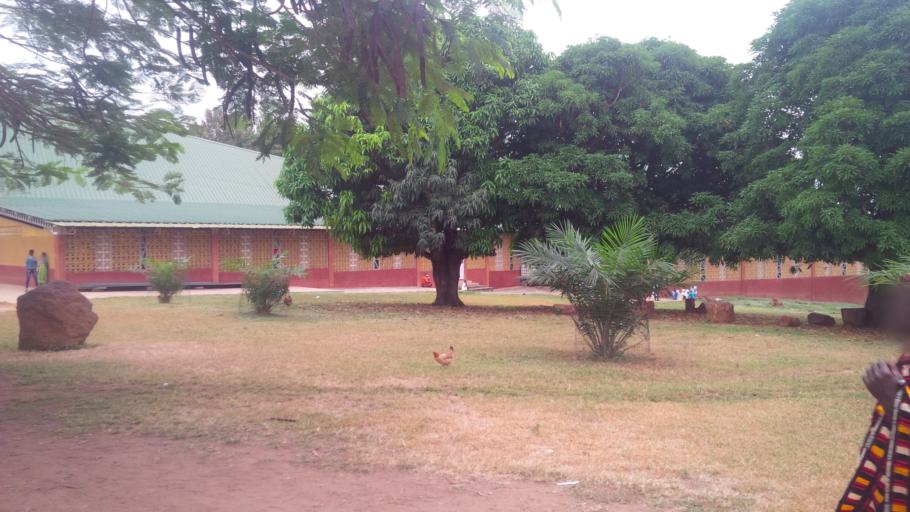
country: CI
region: Zanzan
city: Tanda
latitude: 7.8003
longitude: -3.1639
